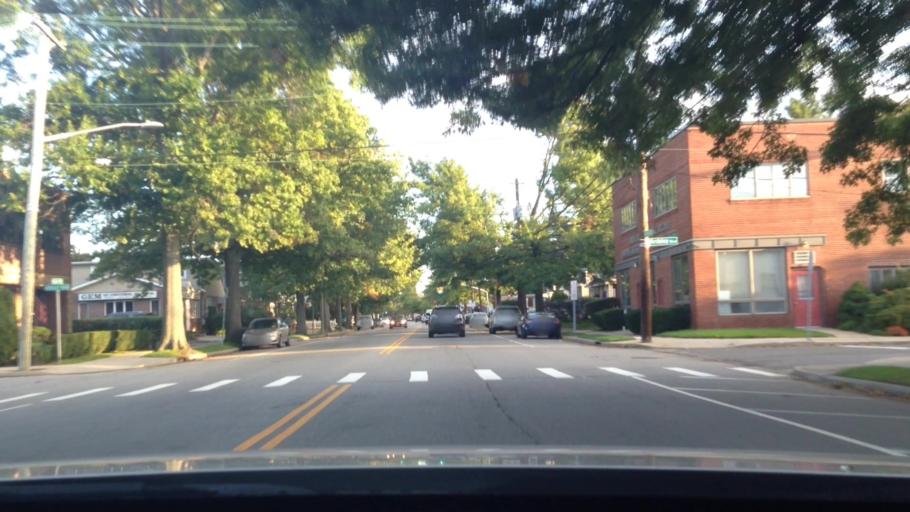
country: US
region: New York
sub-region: Nassau County
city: Garden City South
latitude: 40.7123
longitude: -73.6610
